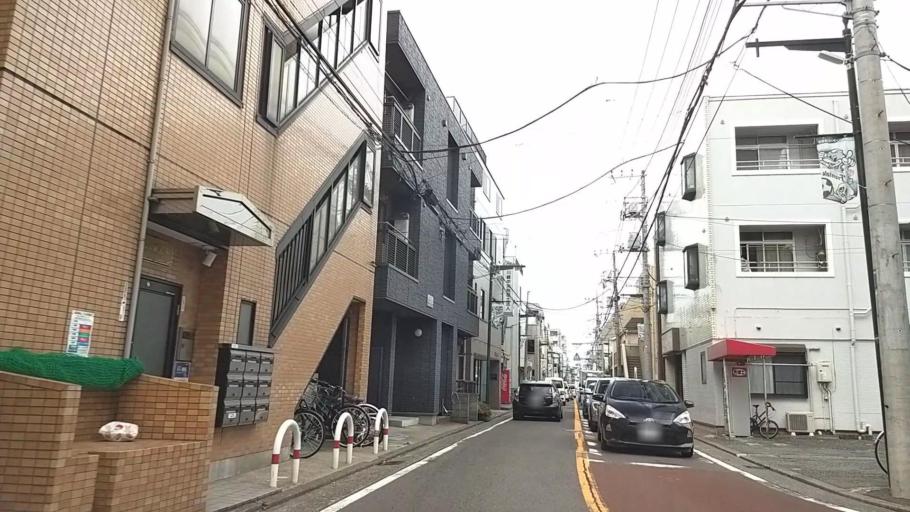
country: JP
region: Kanagawa
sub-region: Kawasaki-shi
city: Kawasaki
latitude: 35.5823
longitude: 139.6548
